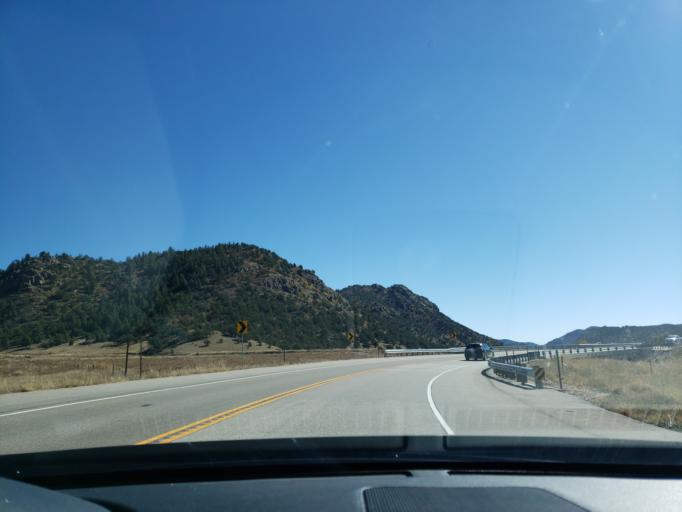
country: US
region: Colorado
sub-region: Fremont County
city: Canon City
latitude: 38.6181
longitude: -105.4457
